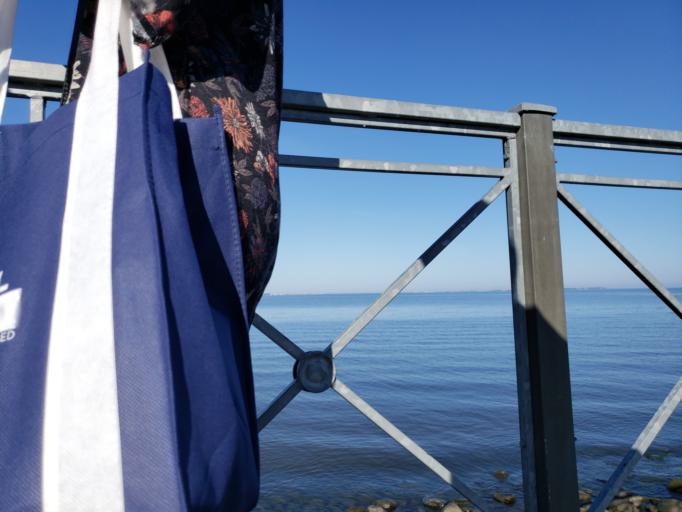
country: RU
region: St.-Petersburg
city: Peterhof
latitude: 59.8910
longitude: 29.9115
